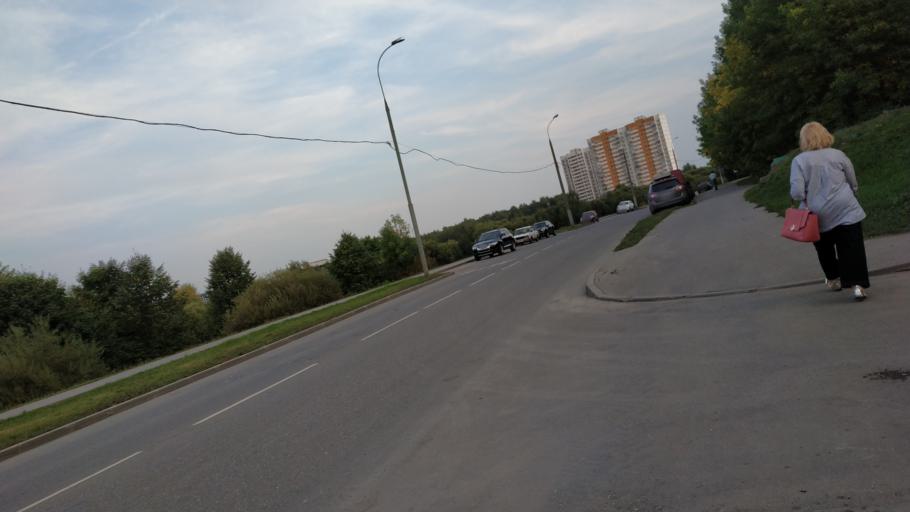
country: RU
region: Moscow
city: Solntsevo
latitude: 55.6430
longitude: 37.3728
